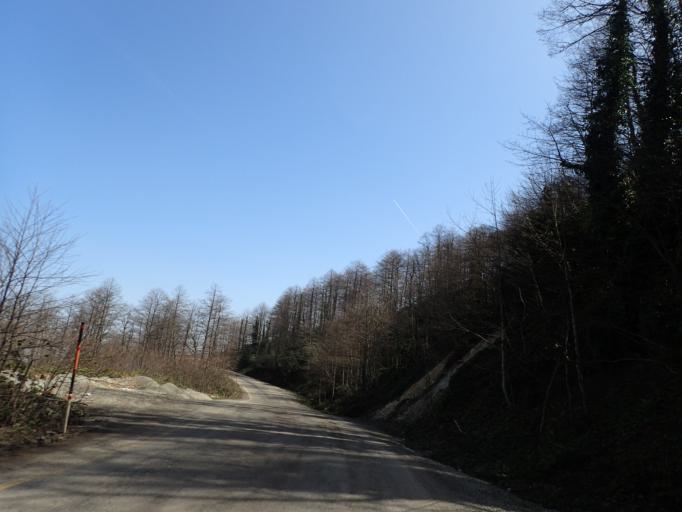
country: TR
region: Ordu
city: Kabaduz
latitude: 40.8239
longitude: 37.8976
